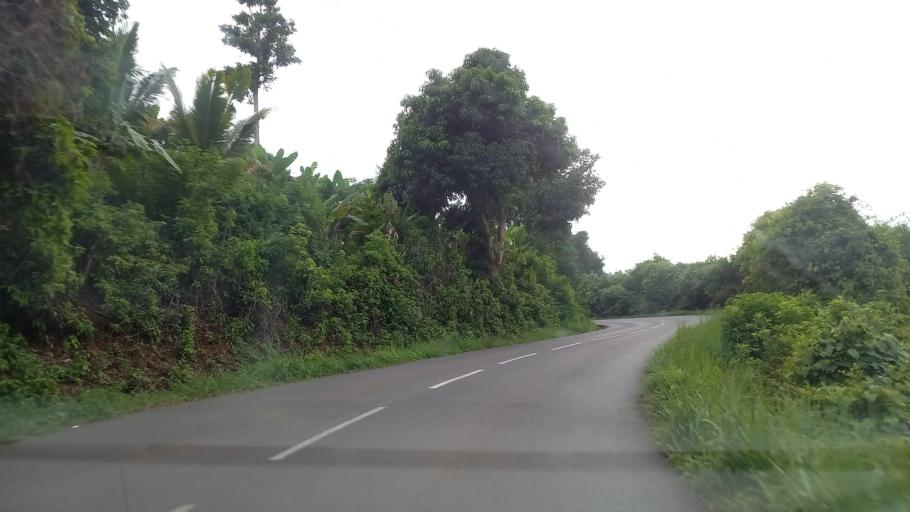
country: YT
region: Bandraboua
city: Bandraboua
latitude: -12.7405
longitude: 45.1177
